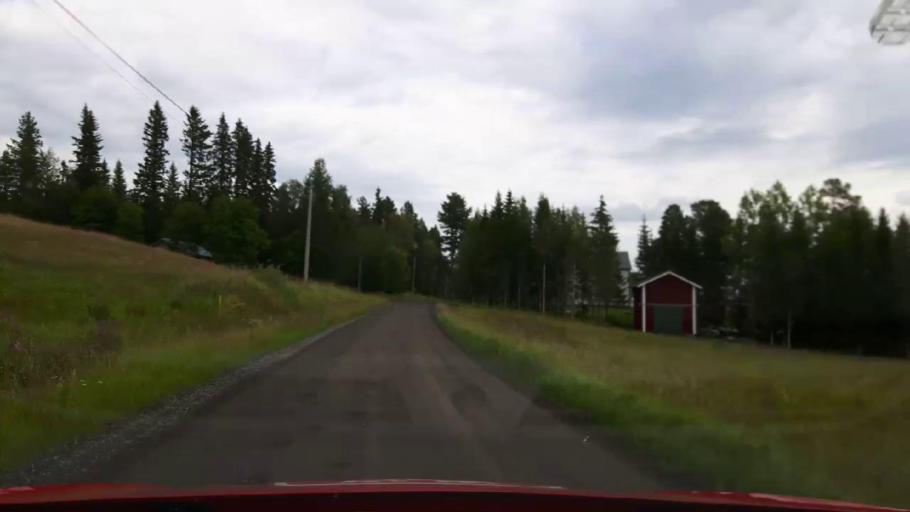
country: SE
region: Jaemtland
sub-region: OEstersunds Kommun
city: Lit
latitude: 63.4471
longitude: 15.2710
